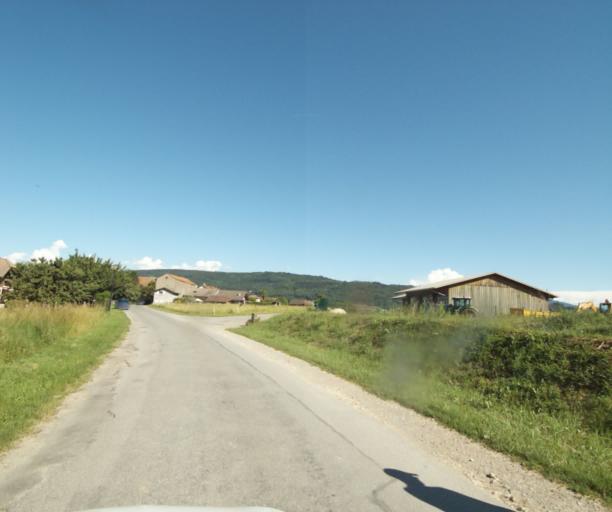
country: FR
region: Rhone-Alpes
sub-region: Departement de la Haute-Savoie
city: Massongy
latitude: 46.3248
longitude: 6.3175
